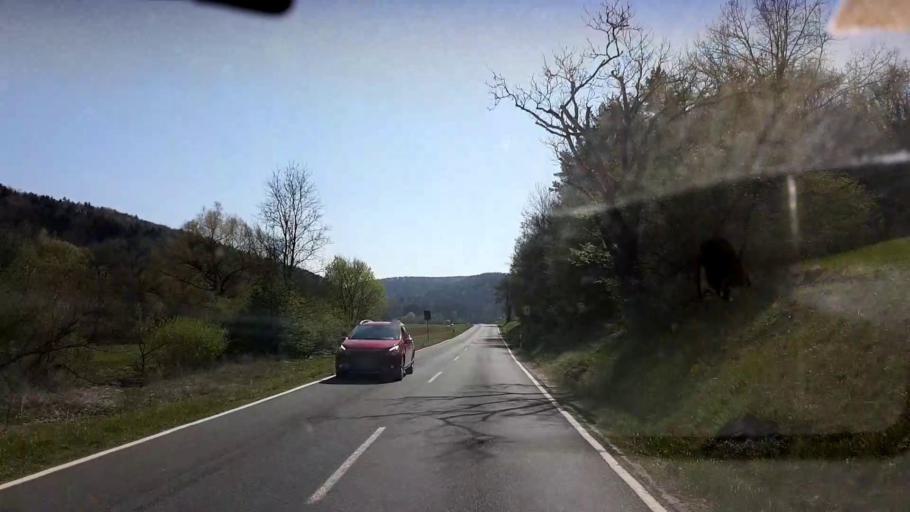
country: DE
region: Bavaria
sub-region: Upper Franconia
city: Unterleinleiter
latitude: 49.8394
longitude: 11.1936
